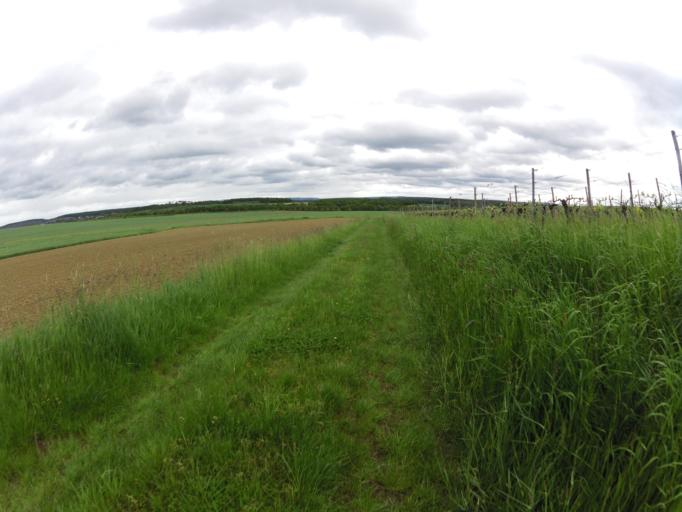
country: DE
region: Bavaria
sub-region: Regierungsbezirk Unterfranken
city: Sommerach
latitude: 49.8420
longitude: 10.2172
